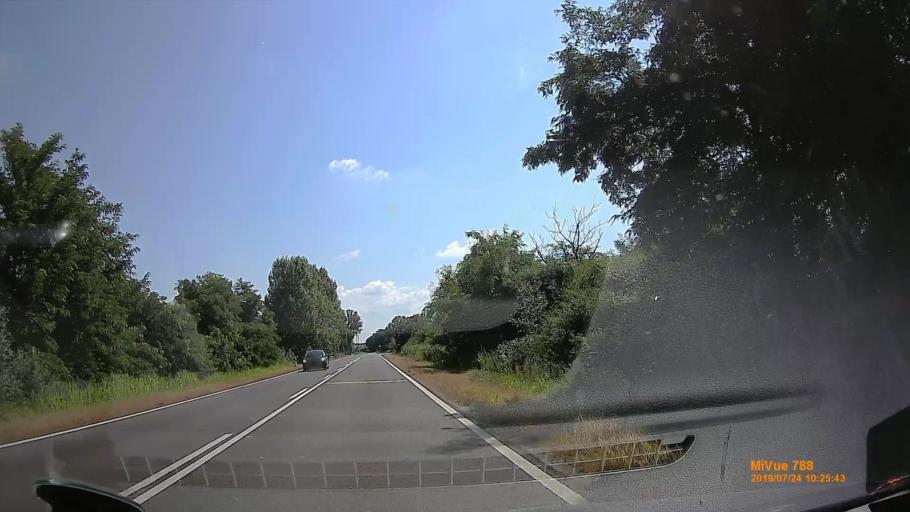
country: HU
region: Szabolcs-Szatmar-Bereg
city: Vasarosnameny
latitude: 48.1523
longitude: 22.4142
